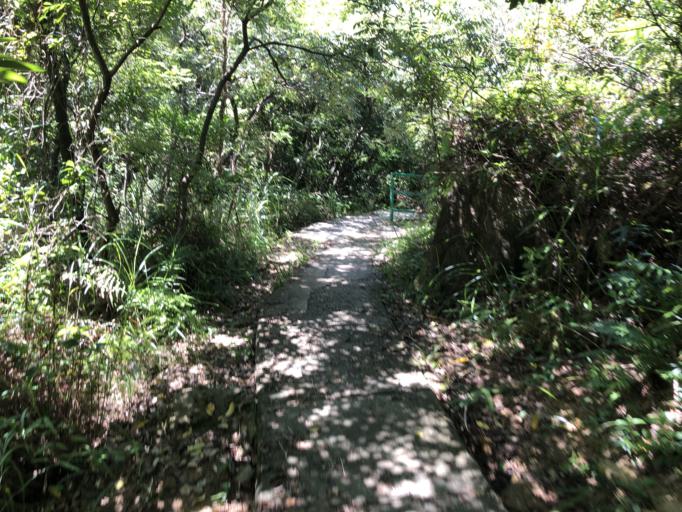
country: HK
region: Tuen Mun
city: Tuen Mun
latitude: 22.2827
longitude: 113.9830
